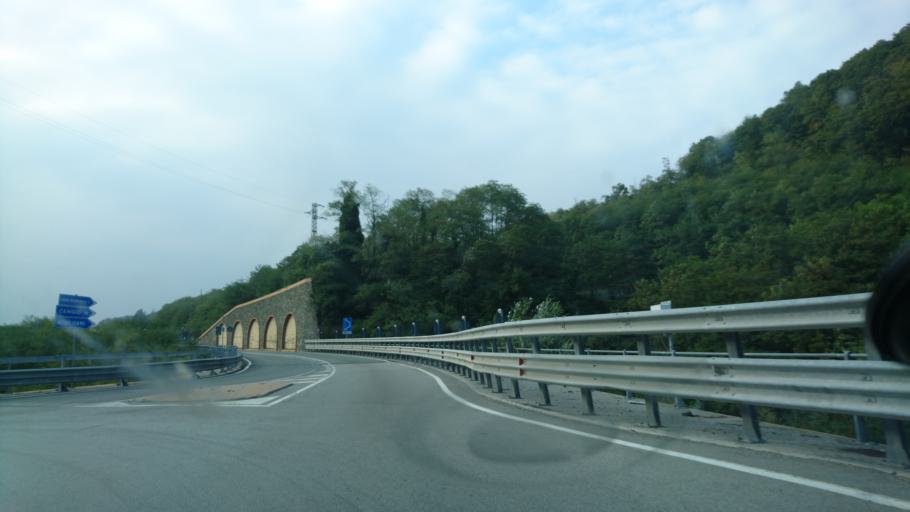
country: IT
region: Liguria
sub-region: Provincia di Savona
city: Altare
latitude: 44.3458
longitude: 8.3209
